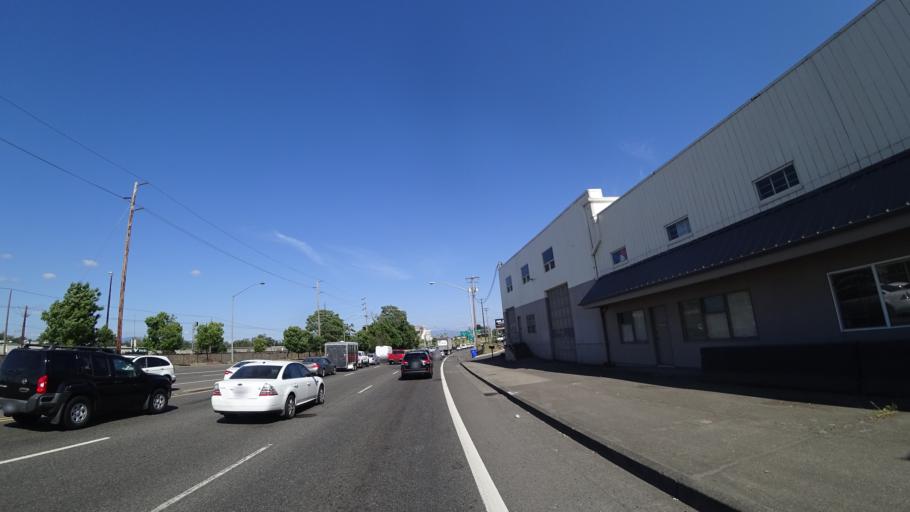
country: US
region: Oregon
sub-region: Multnomah County
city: Lents
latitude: 45.5626
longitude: -122.5709
